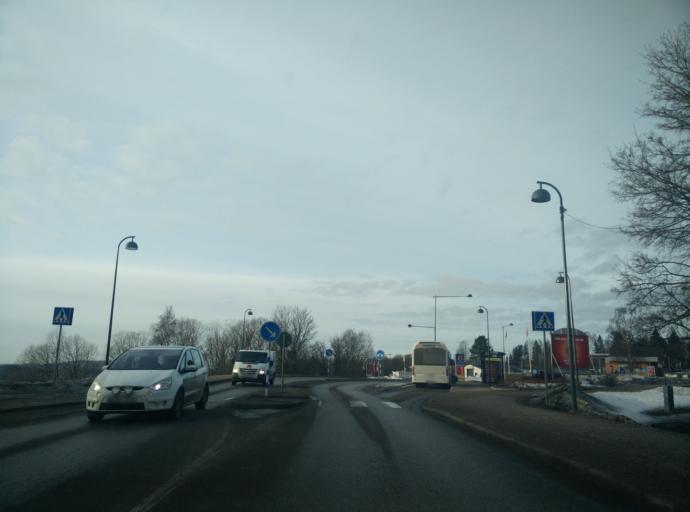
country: SE
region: Vaesternorrland
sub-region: Sundsvalls Kommun
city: Johannedal
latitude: 62.4308
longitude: 17.4162
